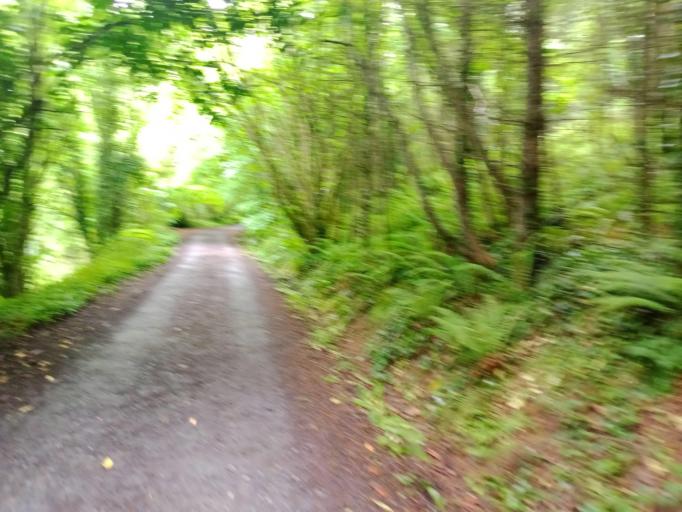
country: IE
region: Leinster
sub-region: Kilkenny
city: Thomastown
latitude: 52.4814
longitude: -7.0486
